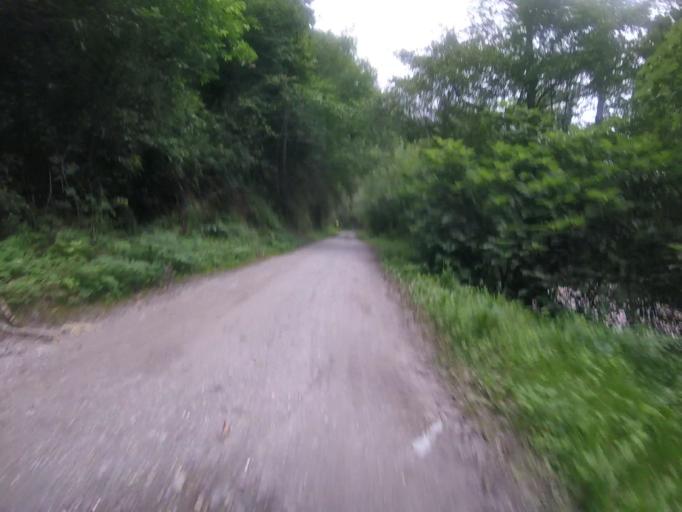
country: ES
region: Navarre
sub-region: Provincia de Navarra
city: Sunbilla
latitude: 43.1950
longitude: -1.6705
